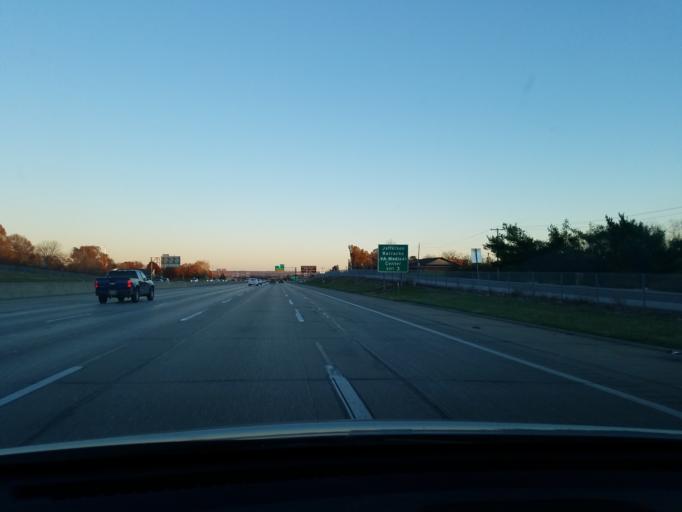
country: US
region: Missouri
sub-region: Saint Louis County
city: Mehlville
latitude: 38.5000
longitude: -90.3140
